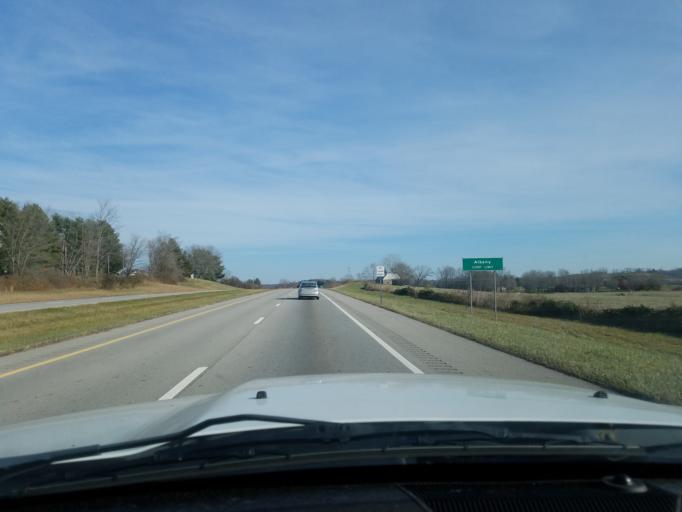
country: US
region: Ohio
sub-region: Athens County
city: Athens
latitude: 39.2213
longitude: -82.2097
